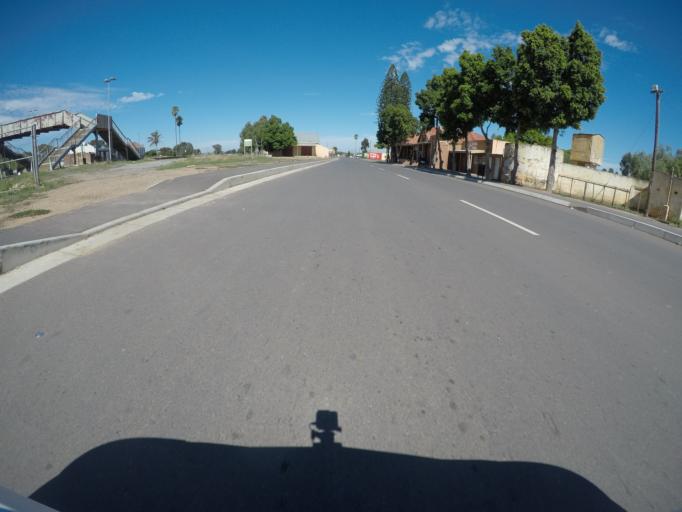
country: ZA
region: Western Cape
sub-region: West Coast District Municipality
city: Malmesbury
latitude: -33.5720
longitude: 18.6470
